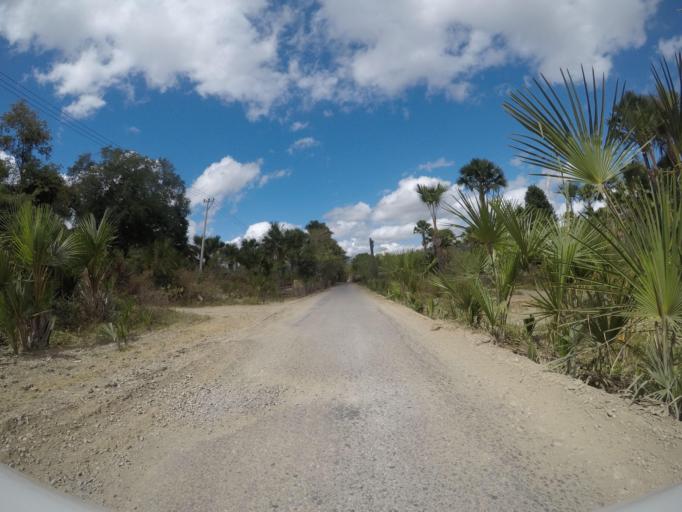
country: TL
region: Lautem
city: Lospalos
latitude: -8.4445
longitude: 126.8248
